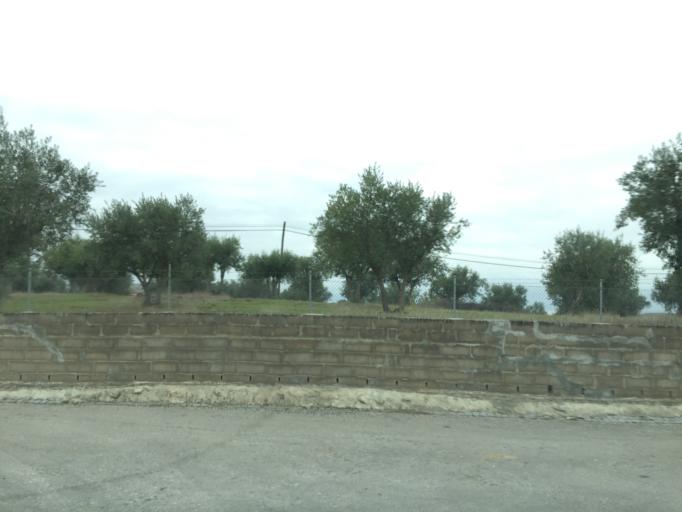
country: PT
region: Portalegre
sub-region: Fronteira
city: Vale da Amoreira
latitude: 39.0477
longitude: -7.7625
